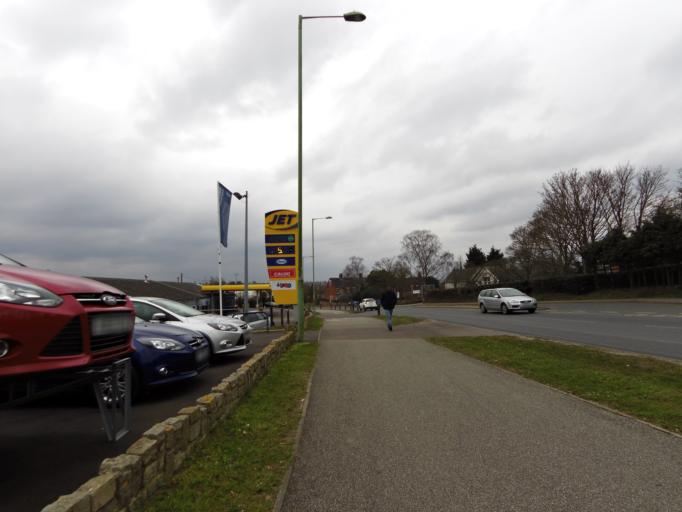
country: GB
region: England
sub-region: Suffolk
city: Halesworth
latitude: 52.3475
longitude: 1.5040
